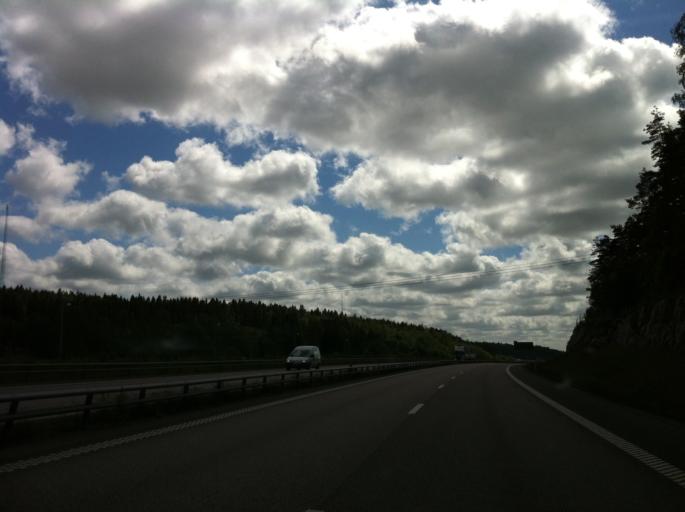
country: SE
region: Vaestra Goetaland
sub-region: Ale Kommun
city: Alvangen
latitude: 57.9482
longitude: 12.0997
